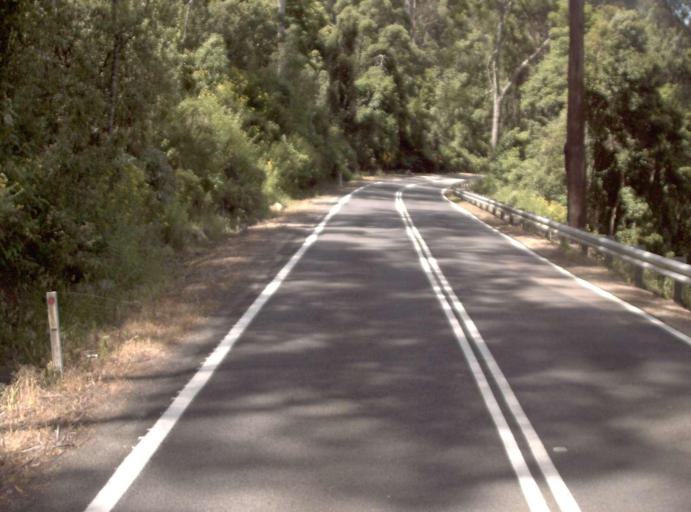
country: AU
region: New South Wales
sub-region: Bombala
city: Bombala
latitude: -37.5624
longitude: 149.3487
